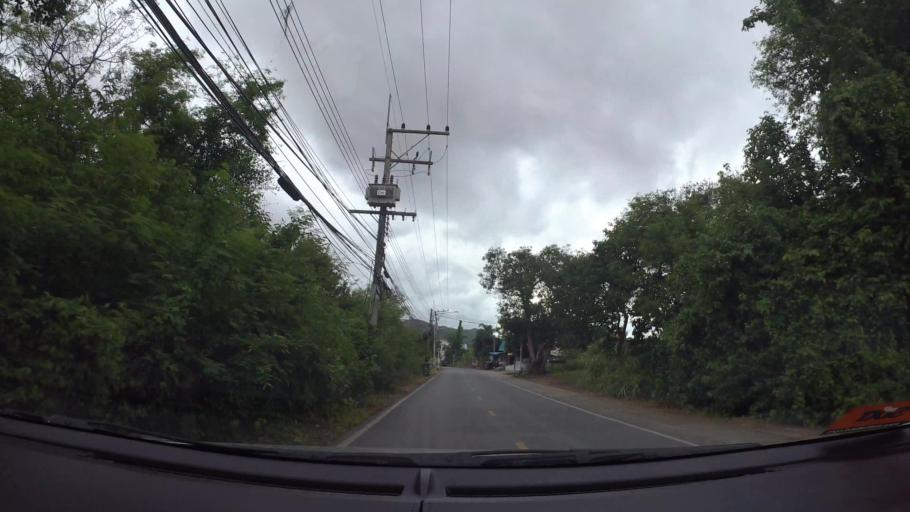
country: TH
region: Chon Buri
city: Sattahip
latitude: 12.7252
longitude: 100.9001
